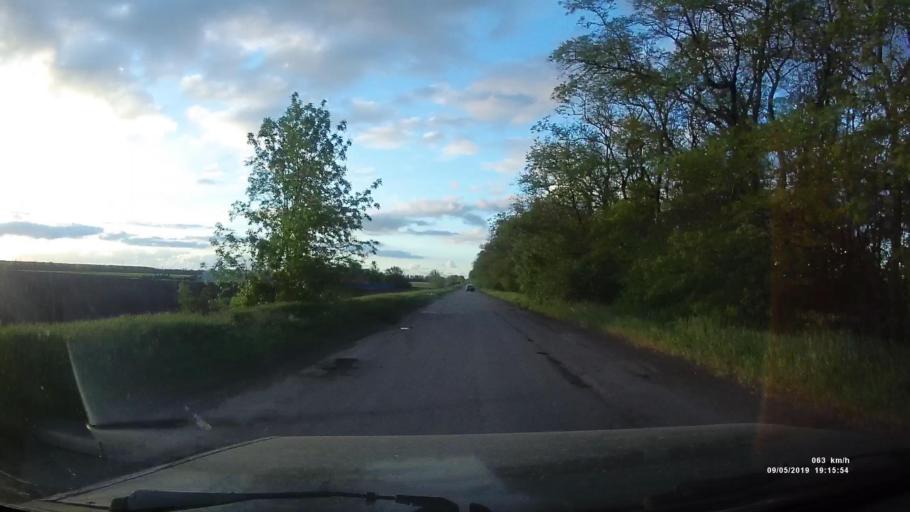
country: RU
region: Krasnodarskiy
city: Kanelovskaya
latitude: 46.7729
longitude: 39.2114
